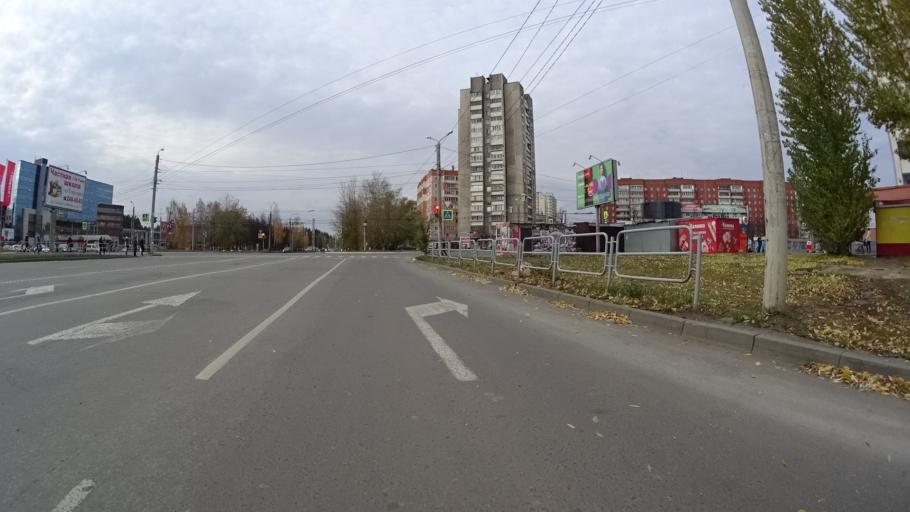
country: RU
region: Chelyabinsk
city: Roshchino
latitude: 55.1933
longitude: 61.3023
